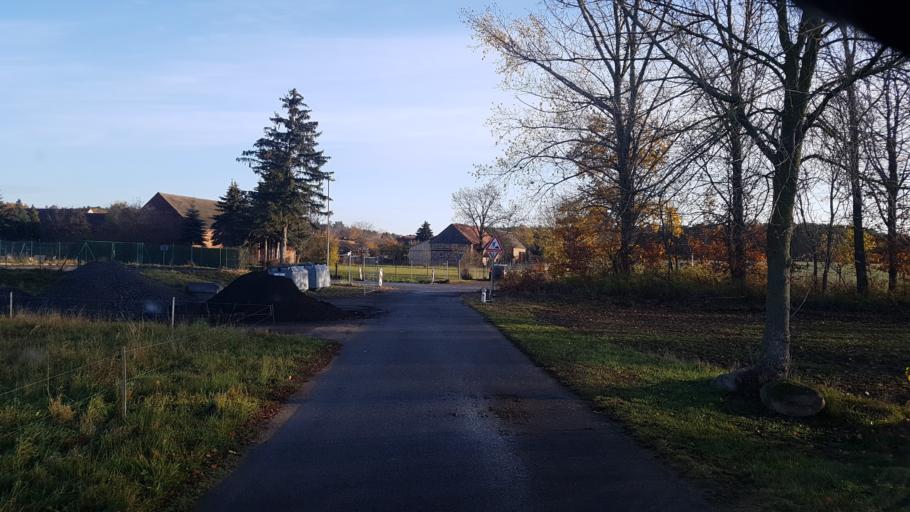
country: DE
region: Brandenburg
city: Crinitz
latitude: 51.7049
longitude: 13.7190
